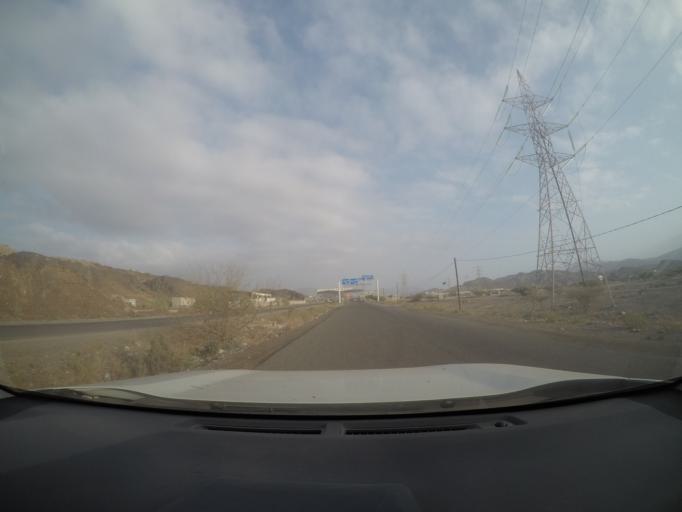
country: YE
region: Lahij
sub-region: Al Milah
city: Al Milah
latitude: 13.2827
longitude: 44.7565
